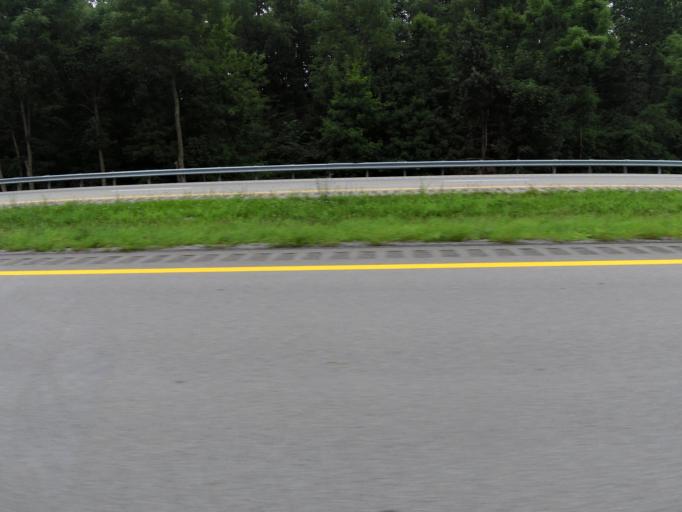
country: US
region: Kentucky
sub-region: Ohio County
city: Oak Grove
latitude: 37.4104
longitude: -86.5344
